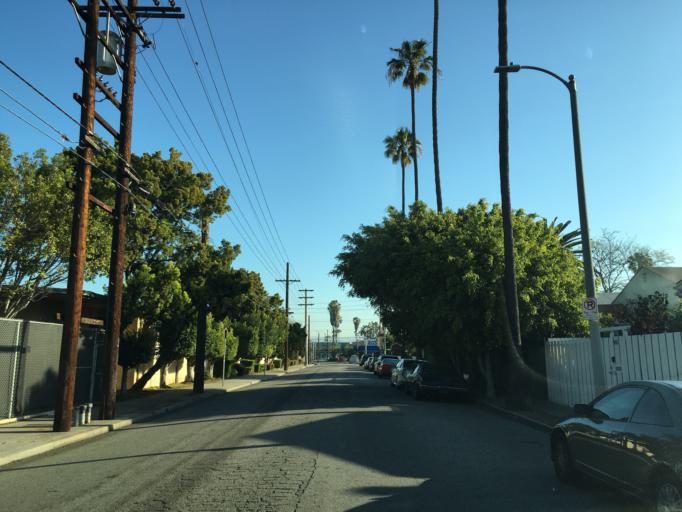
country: US
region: California
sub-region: Los Angeles County
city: Marina del Rey
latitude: 33.9966
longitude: -118.4619
